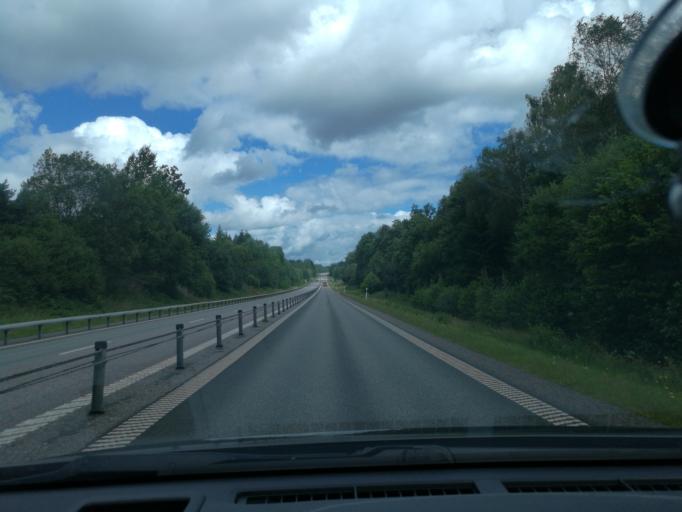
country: SE
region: Skane
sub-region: Hassleholms Kommun
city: Hastveda
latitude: 56.2358
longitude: 13.8988
